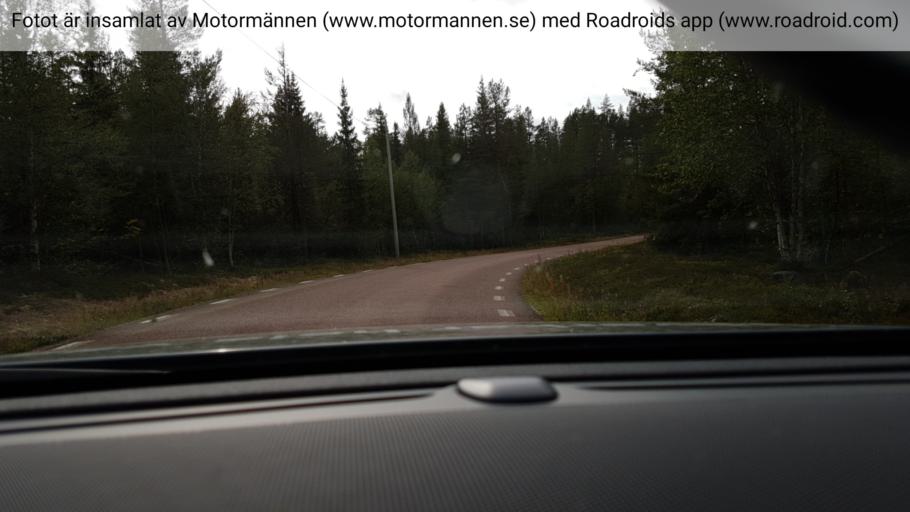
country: NO
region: Hedmark
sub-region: Trysil
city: Innbygda
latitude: 61.6916
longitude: 12.6004
